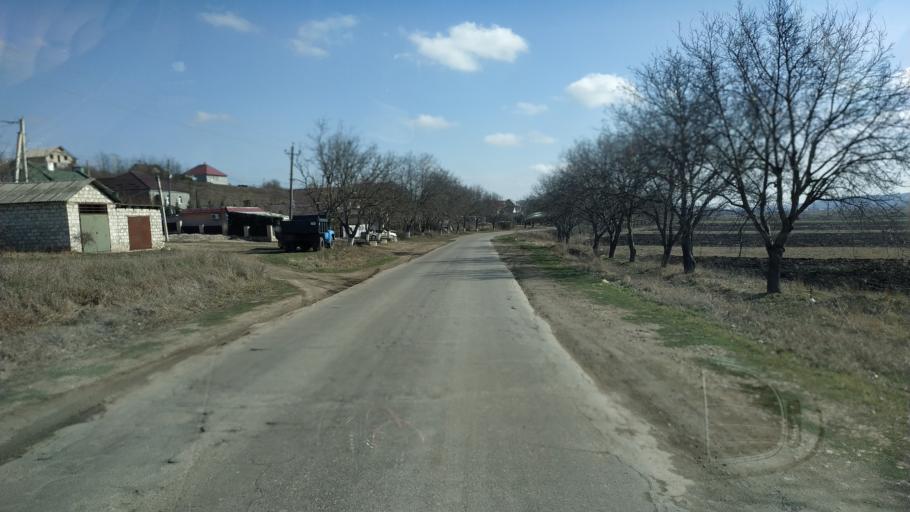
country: MD
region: Laloveni
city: Ialoveni
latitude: 46.9308
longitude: 28.6679
